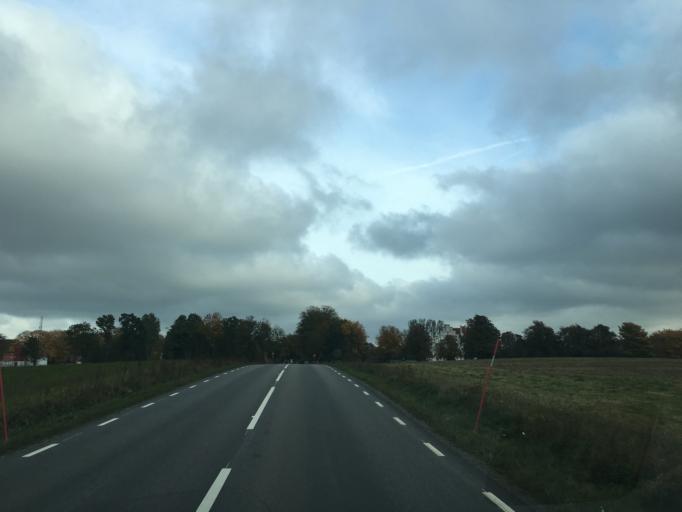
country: SE
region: Skane
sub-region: Simrishamns Kommun
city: Kivik
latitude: 55.6350
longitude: 14.1180
